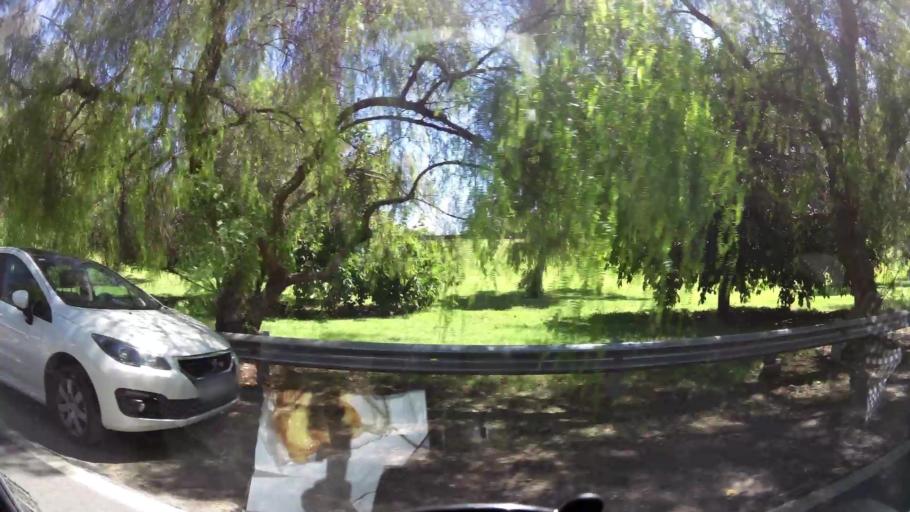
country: AR
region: San Juan
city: San Juan
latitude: -31.5202
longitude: -68.5347
